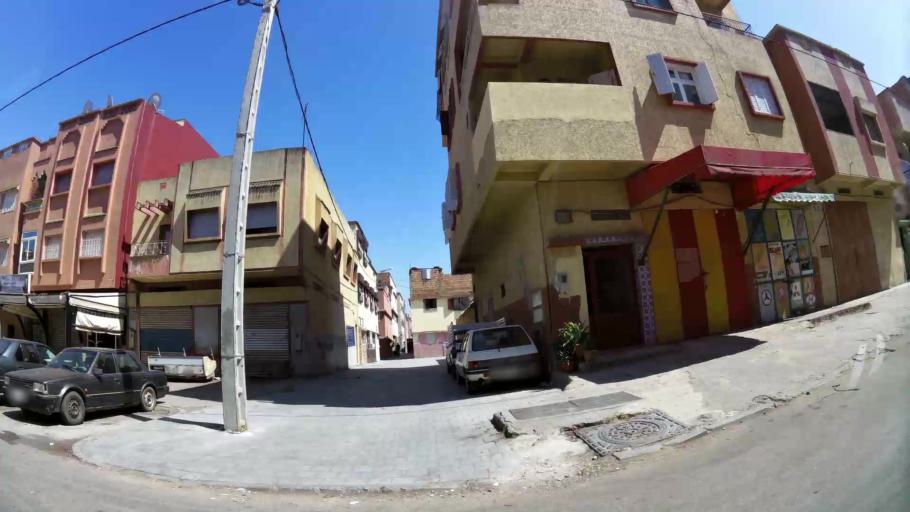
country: MA
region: Gharb-Chrarda-Beni Hssen
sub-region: Kenitra Province
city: Kenitra
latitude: 34.2449
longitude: -6.5532
